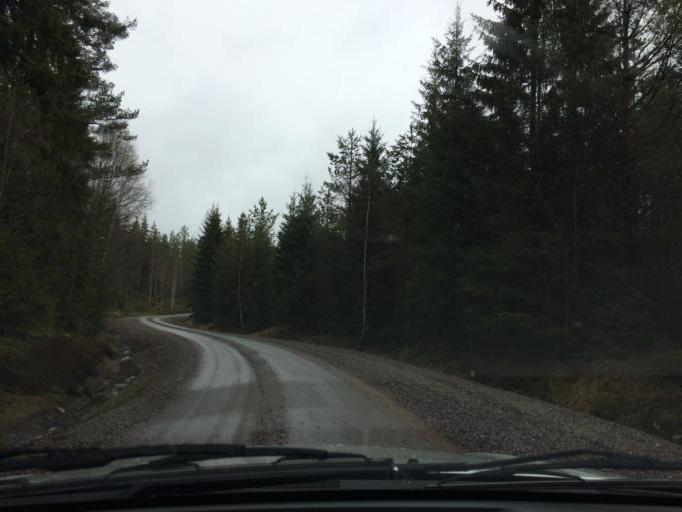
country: SE
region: Dalarna
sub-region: Ludvika Kommun
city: Abborrberget
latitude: 60.0201
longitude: 14.6101
